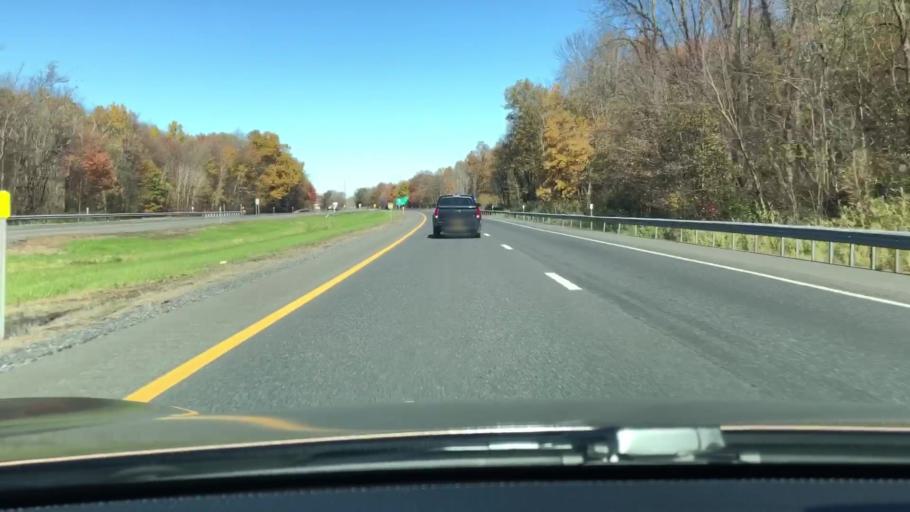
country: US
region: New York
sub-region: Ulster County
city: New Paltz
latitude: 41.7261
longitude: -74.0683
